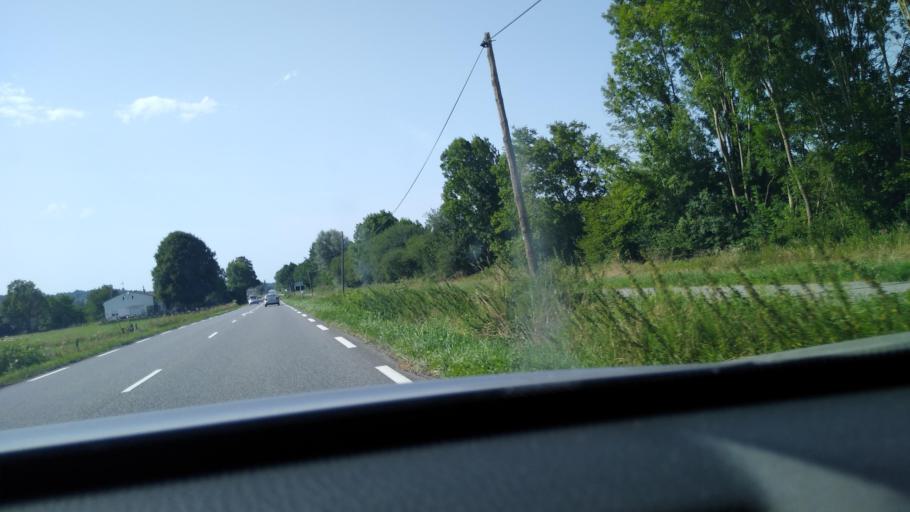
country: FR
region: Midi-Pyrenees
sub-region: Departement de la Haute-Garonne
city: Salies-du-Salat
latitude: 43.0454
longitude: 0.9884
